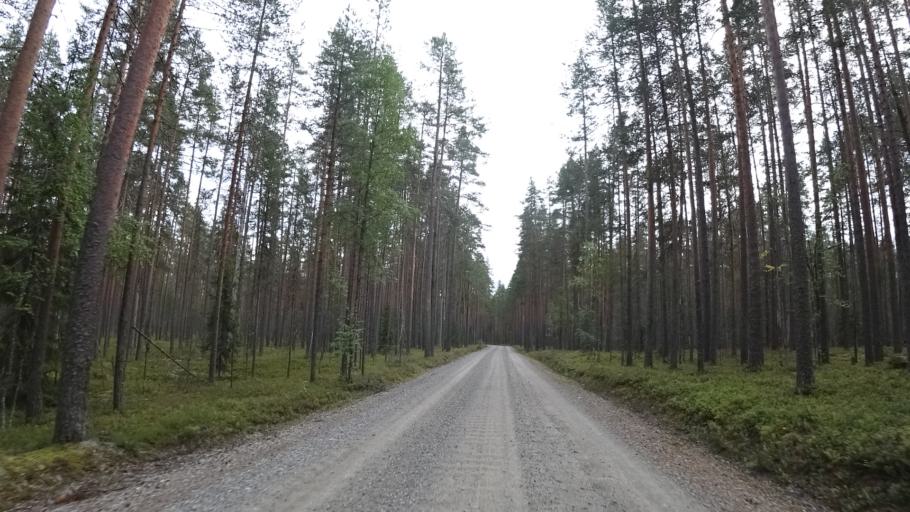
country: FI
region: North Karelia
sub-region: Joensuu
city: Ilomantsi
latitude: 62.6029
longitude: 31.1861
